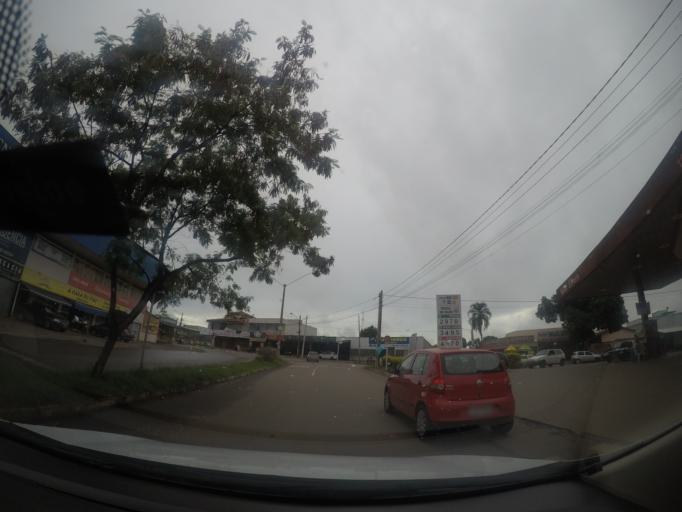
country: BR
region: Goias
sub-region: Aparecida De Goiania
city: Aparecida de Goiania
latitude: -16.7679
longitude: -49.3234
